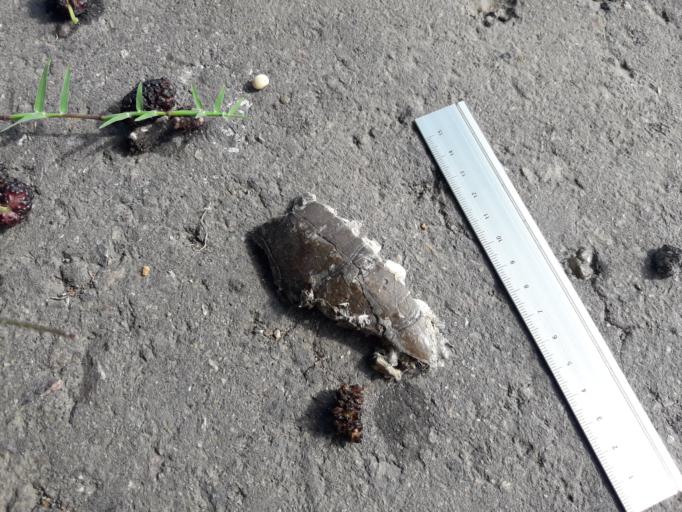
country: AR
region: Santa Fe
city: Santa Fe de la Vera Cruz
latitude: -31.6508
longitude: -60.6161
